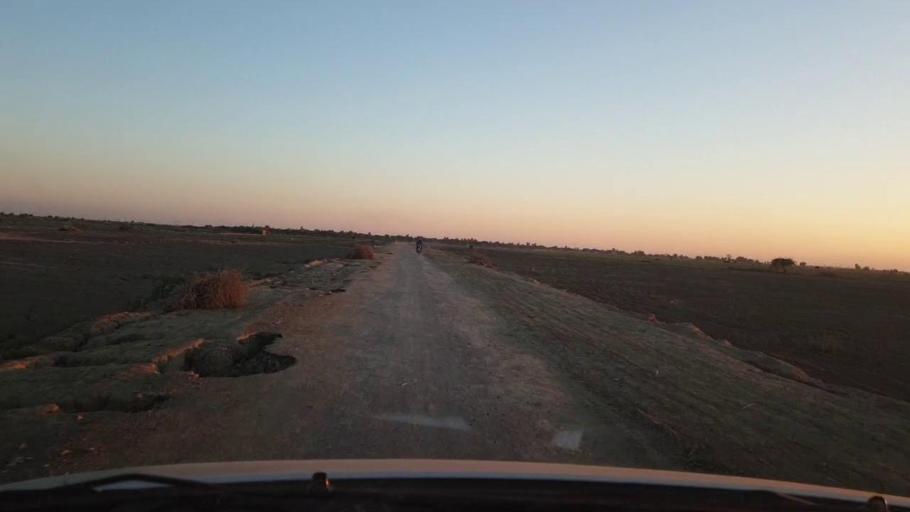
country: PK
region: Sindh
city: Johi
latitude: 26.8407
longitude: 67.4408
